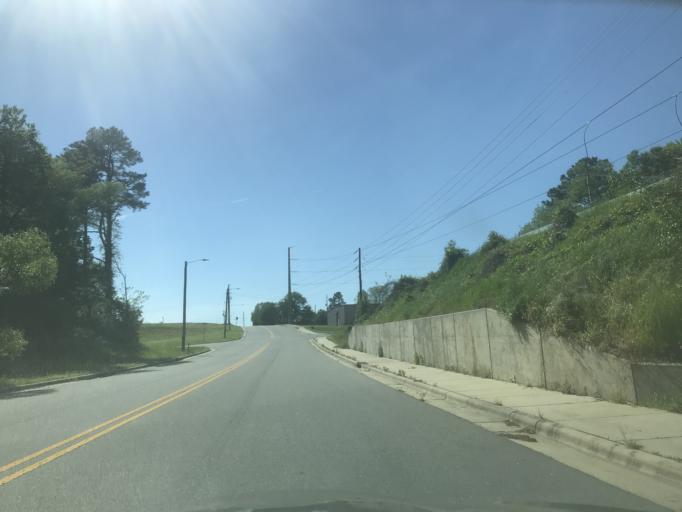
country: US
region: North Carolina
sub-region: Wake County
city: Raleigh
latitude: 35.7580
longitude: -78.6455
